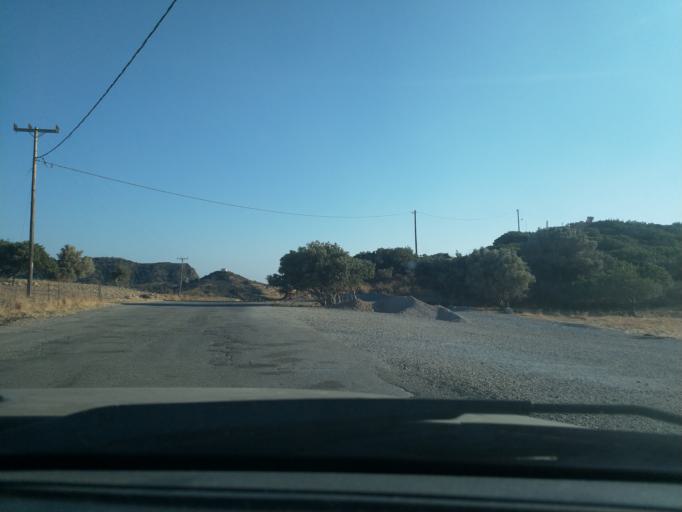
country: GR
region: Crete
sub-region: Nomos Rethymnis
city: Agia Galini
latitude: 35.1215
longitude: 24.5586
